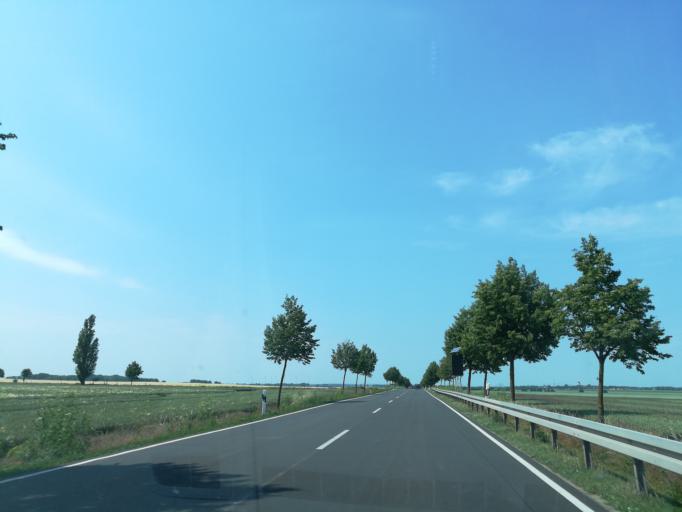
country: DE
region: Saxony-Anhalt
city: Schneidlingen
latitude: 51.9079
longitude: 11.4325
